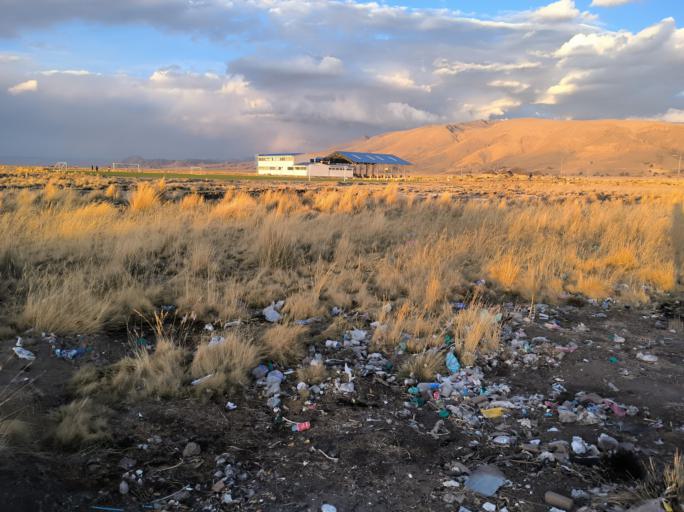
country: BO
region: Oruro
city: Challapata
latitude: -19.0092
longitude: -66.8206
